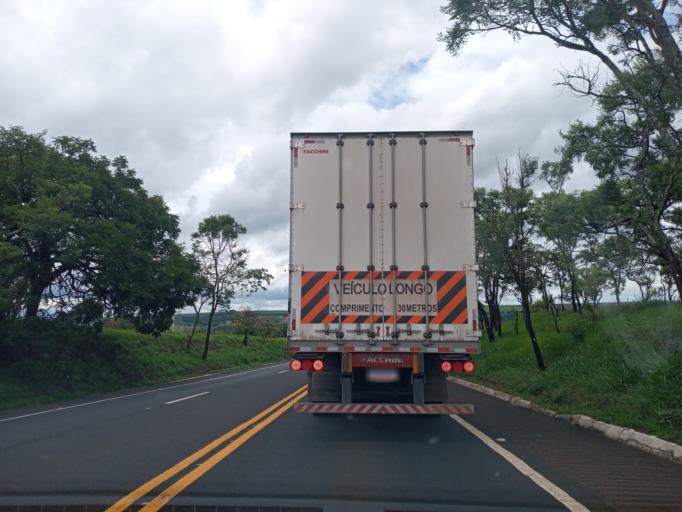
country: BR
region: Minas Gerais
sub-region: Uberaba
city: Uberaba
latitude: -19.2869
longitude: -47.6213
